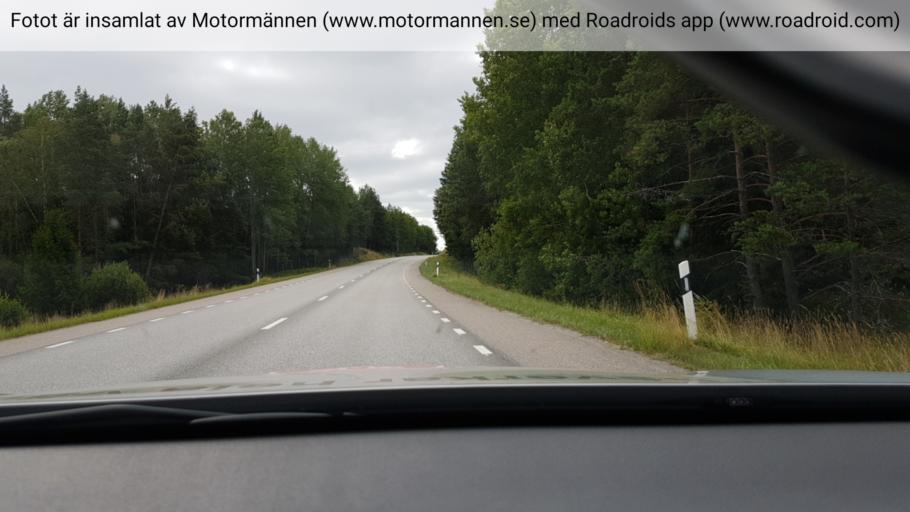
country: SE
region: Stockholm
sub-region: Norrtalje Kommun
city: Rimbo
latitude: 59.6422
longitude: 18.3326
